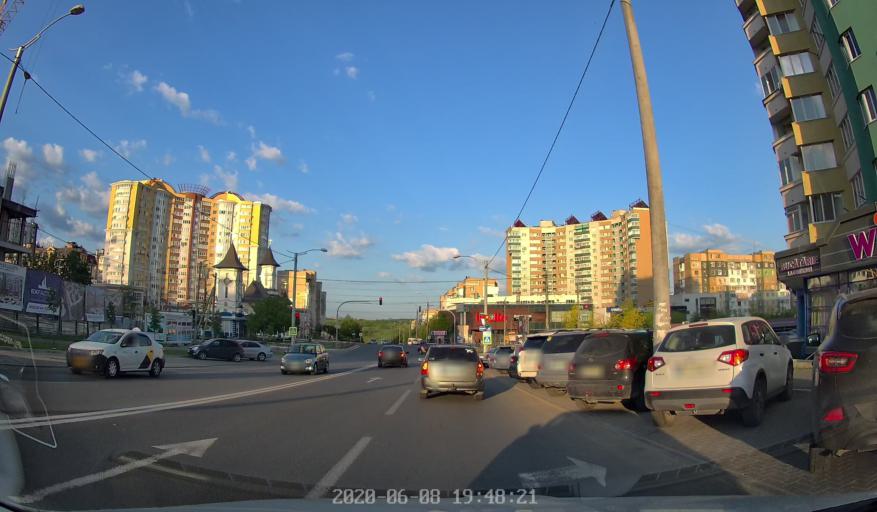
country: MD
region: Chisinau
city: Stauceni
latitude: 47.0565
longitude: 28.8902
